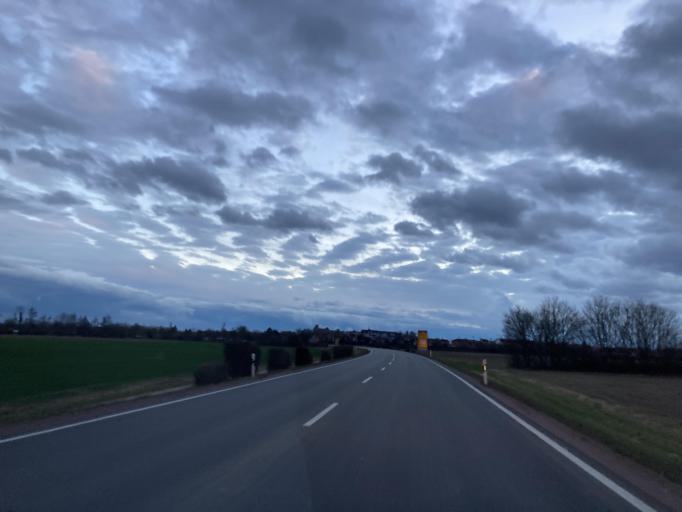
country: DE
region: Baden-Wuerttemberg
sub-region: Freiburg Region
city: Breisach am Rhein
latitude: 48.0480
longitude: 7.5891
